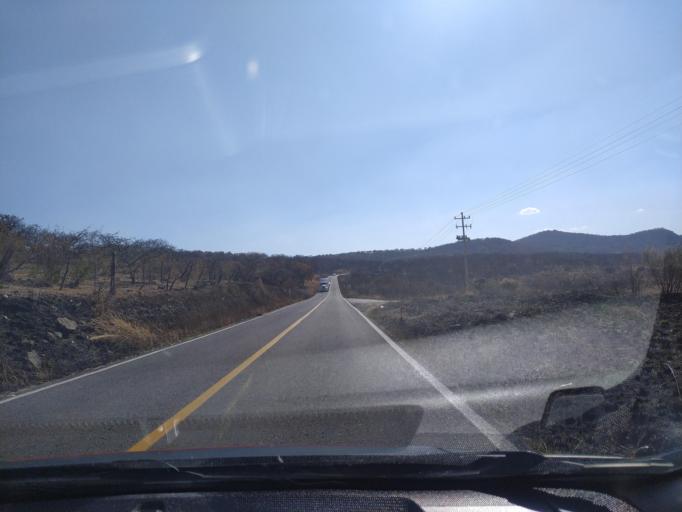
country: MX
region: Guanajuato
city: Ciudad Manuel Doblado
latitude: 20.6281
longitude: -101.9832
